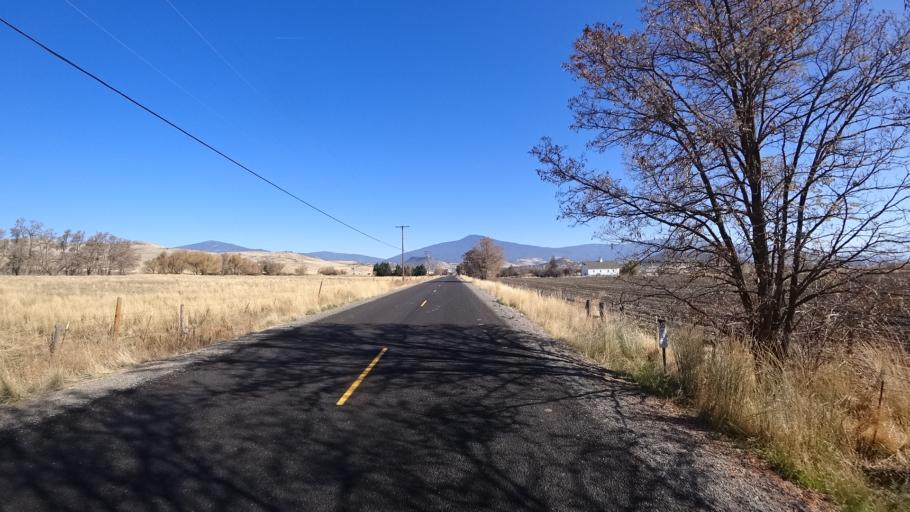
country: US
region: California
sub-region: Siskiyou County
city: Montague
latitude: 41.7262
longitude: -122.4037
